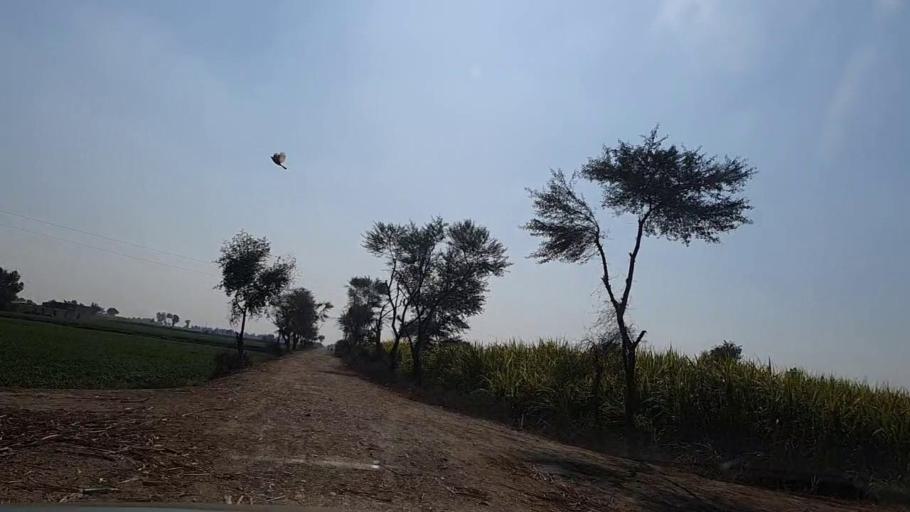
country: PK
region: Sindh
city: Daulatpur
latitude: 26.2877
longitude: 68.0537
